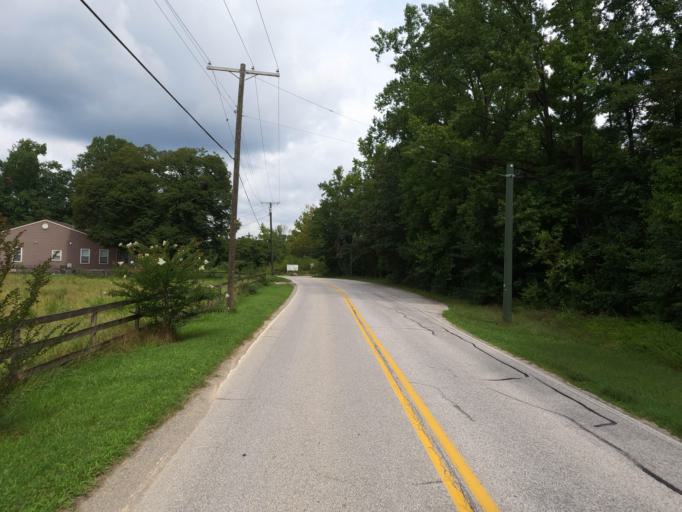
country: US
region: Maryland
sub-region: Anne Arundel County
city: Crofton
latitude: 39.0369
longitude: -76.7154
